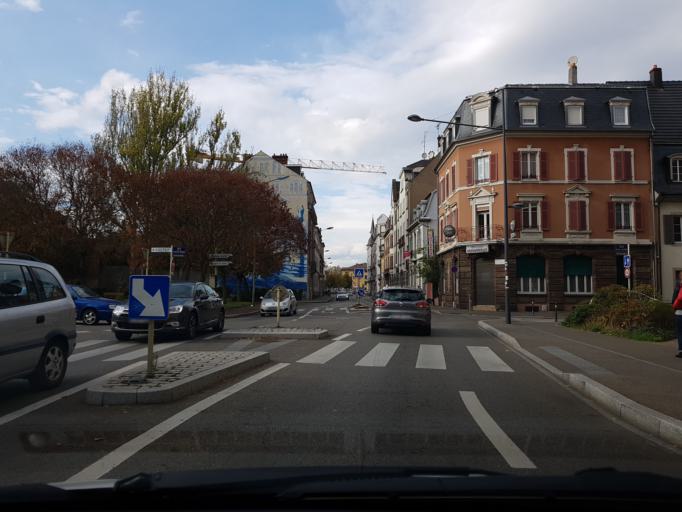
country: FR
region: Alsace
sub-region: Departement du Haut-Rhin
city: Mulhouse
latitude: 47.7442
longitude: 7.3325
